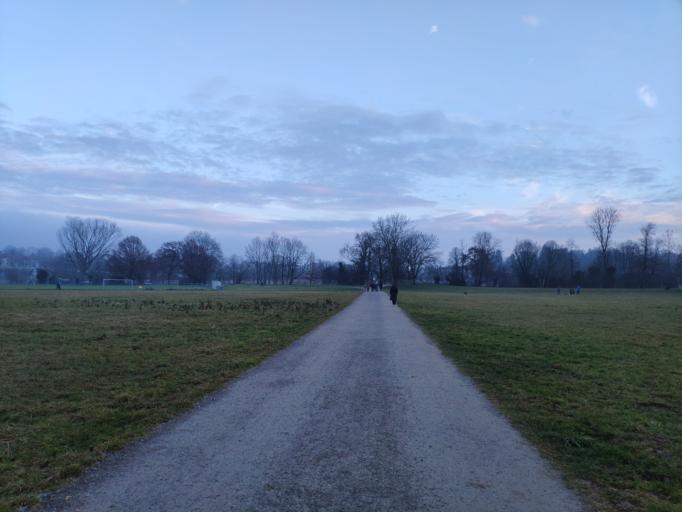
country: CH
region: Zurich
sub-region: Bezirk Zuerich
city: Zuerich (Kreis 3) / Alt-Wiedikon
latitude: 47.3529
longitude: 8.5185
